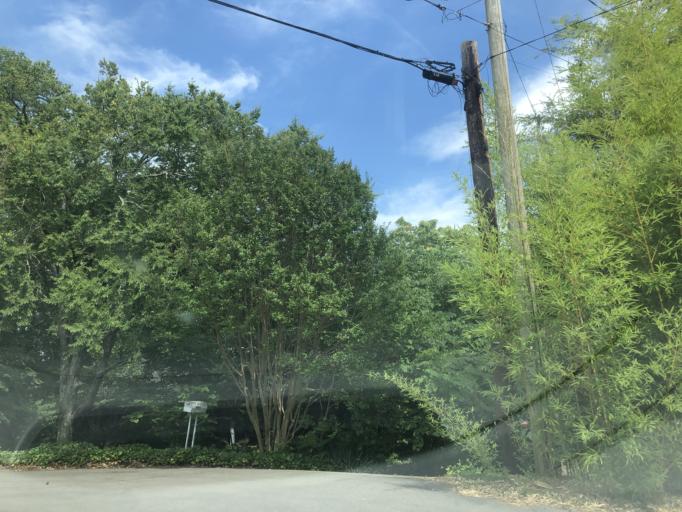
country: US
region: Tennessee
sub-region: Davidson County
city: Belle Meade
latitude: 36.0762
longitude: -86.9339
